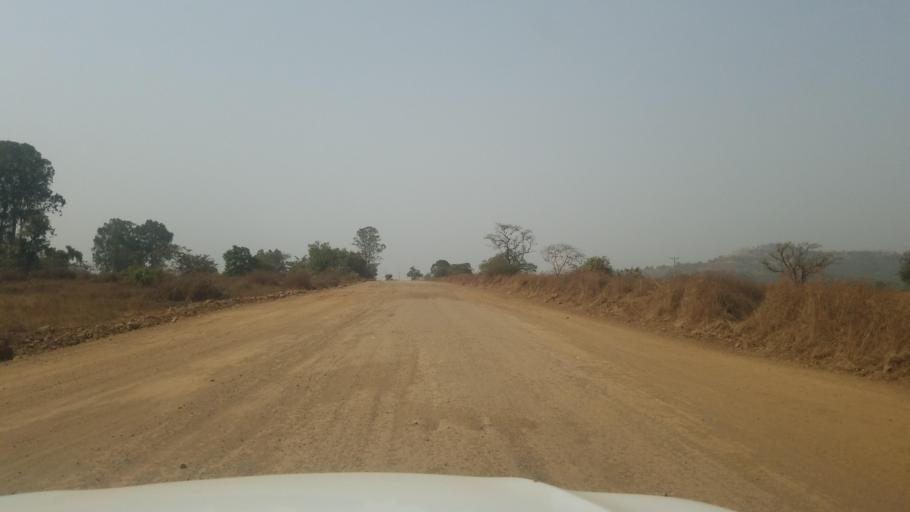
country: ET
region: Amhara
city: Bure
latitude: 10.9330
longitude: 36.4681
